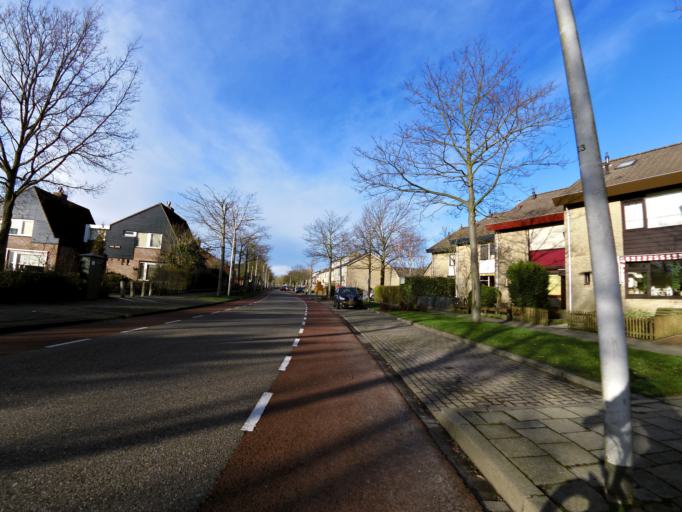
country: NL
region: South Holland
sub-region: Gemeente Hellevoetsluis
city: Nieuw-Helvoet
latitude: 51.8687
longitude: 4.0717
